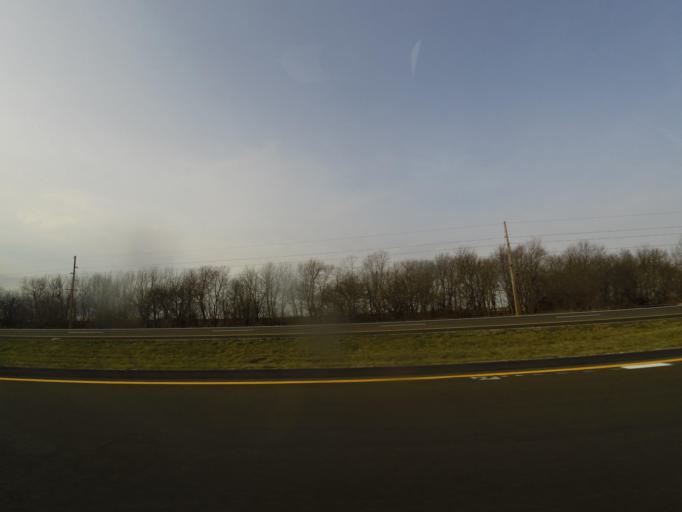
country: US
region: Illinois
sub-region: Christian County
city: Assumption
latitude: 39.5442
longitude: -89.0419
